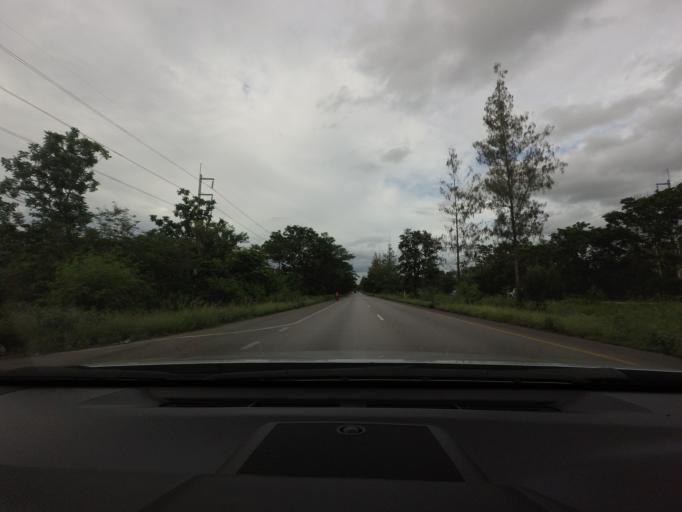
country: TH
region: Phetchaburi
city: Cha-am
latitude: 12.6918
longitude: 99.9014
